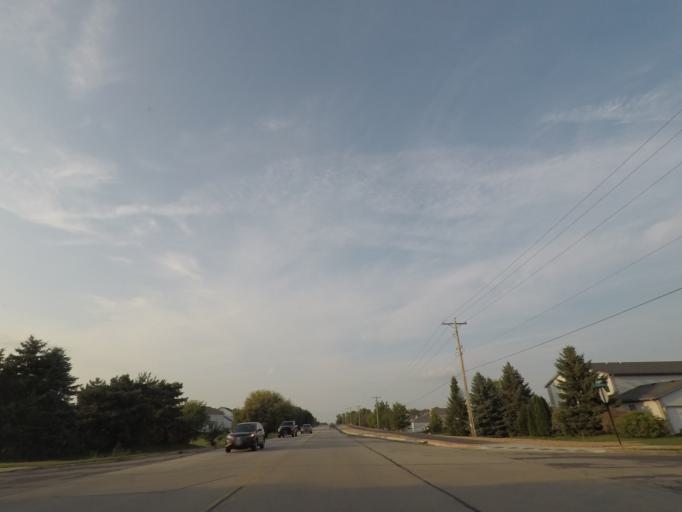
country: US
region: Wisconsin
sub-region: Dane County
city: Cottage Grove
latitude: 43.0936
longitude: -89.1995
